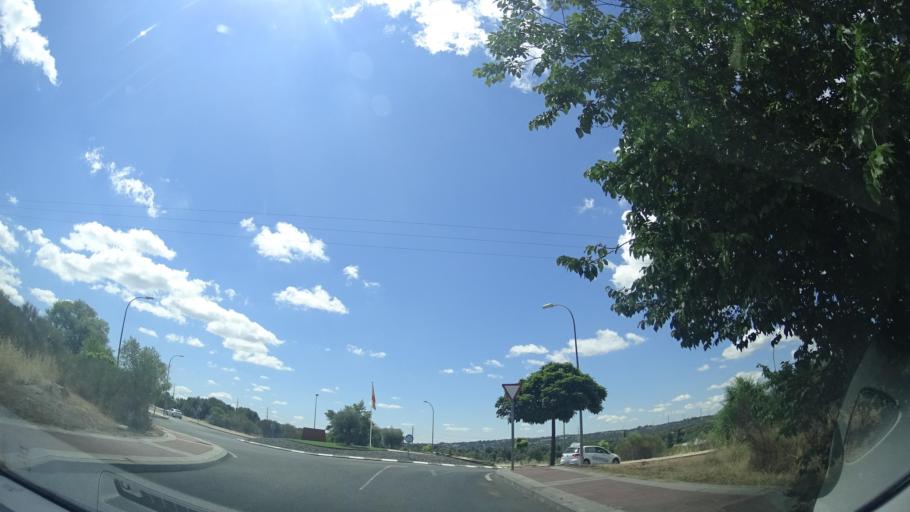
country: ES
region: Madrid
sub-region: Provincia de Madrid
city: Collado-Villalba
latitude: 40.6208
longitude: -3.9920
